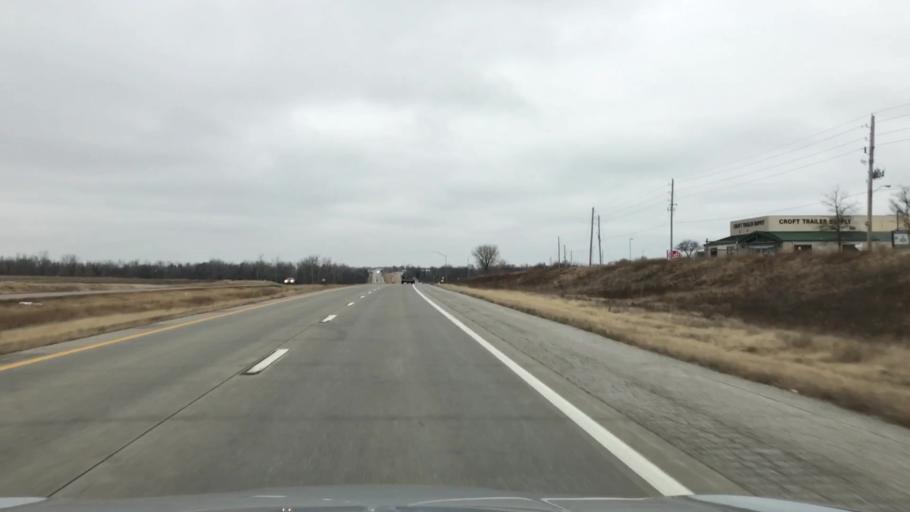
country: US
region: Missouri
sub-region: Jackson County
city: Lees Summit
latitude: 38.8747
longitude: -94.3744
